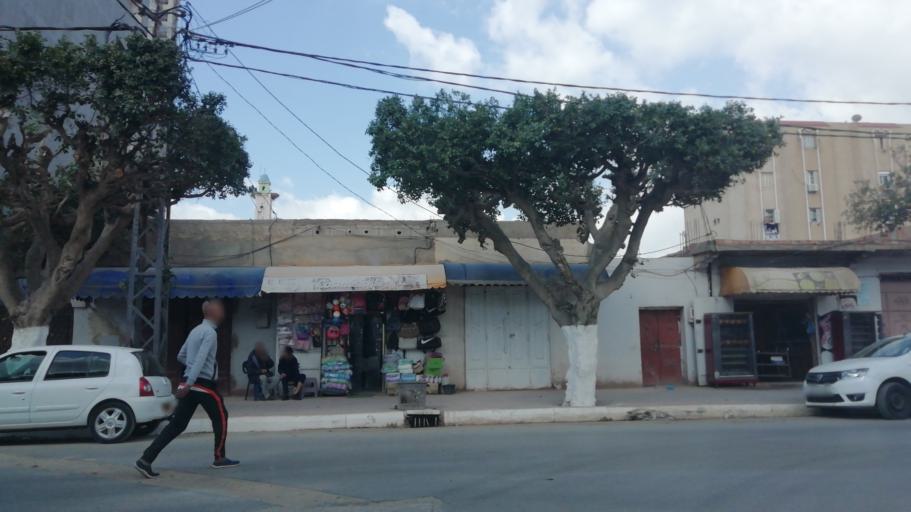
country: DZ
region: Mascara
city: Mascara
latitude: 35.5874
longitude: 0.0685
